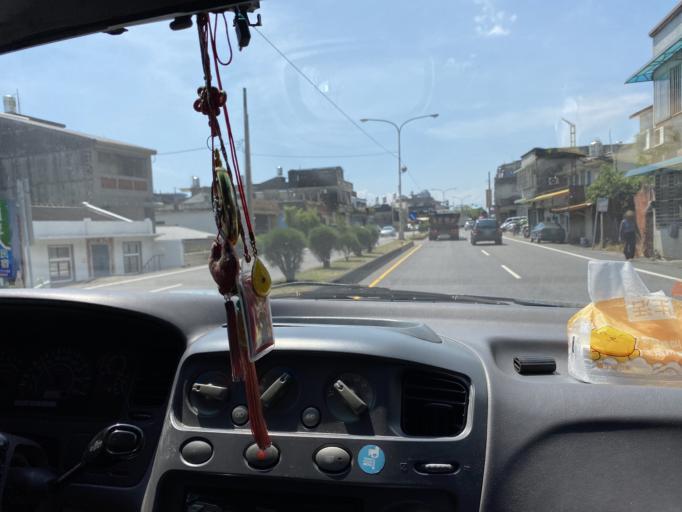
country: TW
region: Taiwan
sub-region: Yilan
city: Yilan
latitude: 24.8762
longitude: 121.8394
